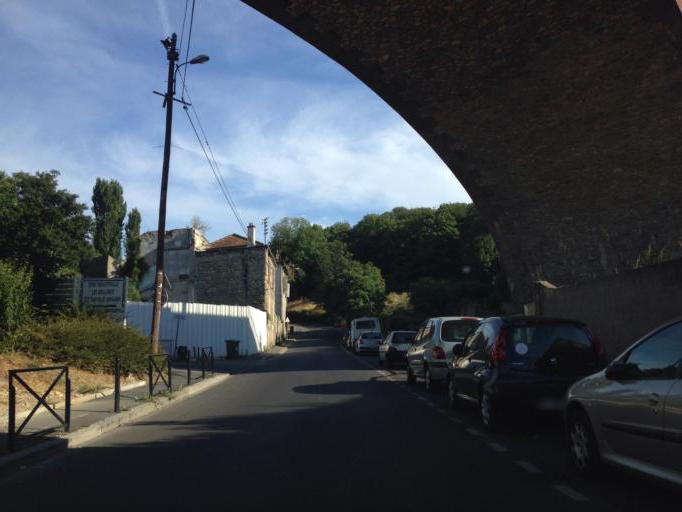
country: FR
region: Ile-de-France
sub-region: Departement des Hauts-de-Seine
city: Meudon
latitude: 48.8152
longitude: 2.2476
